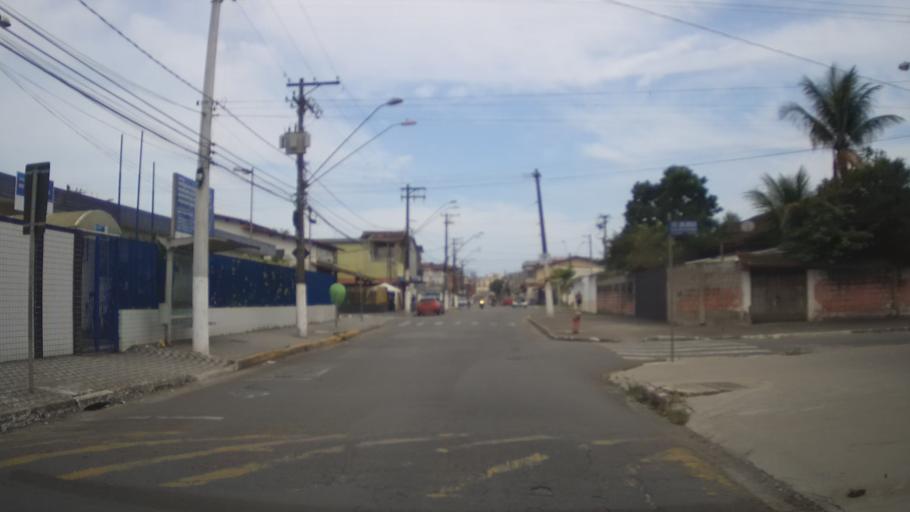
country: BR
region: Sao Paulo
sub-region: Praia Grande
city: Praia Grande
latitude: -24.0025
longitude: -46.4456
